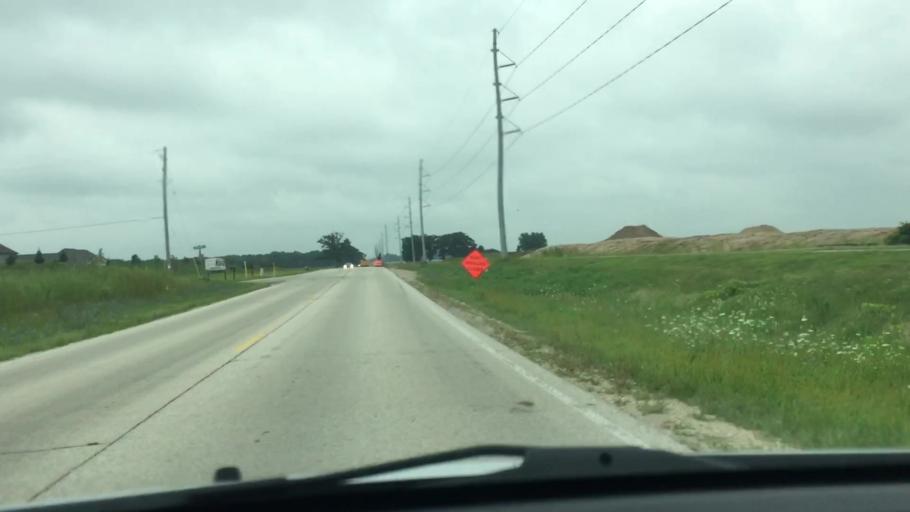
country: US
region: Wisconsin
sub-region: Waukesha County
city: Delafield
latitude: 43.0787
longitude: -88.4419
